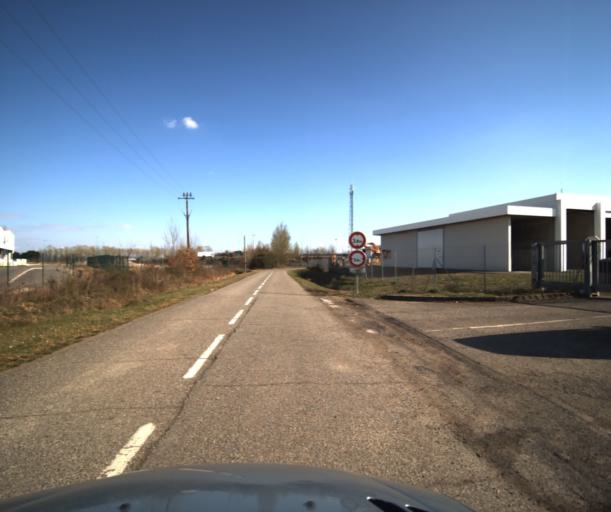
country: FR
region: Midi-Pyrenees
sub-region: Departement du Tarn-et-Garonne
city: Campsas
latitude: 43.9306
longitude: 1.3158
